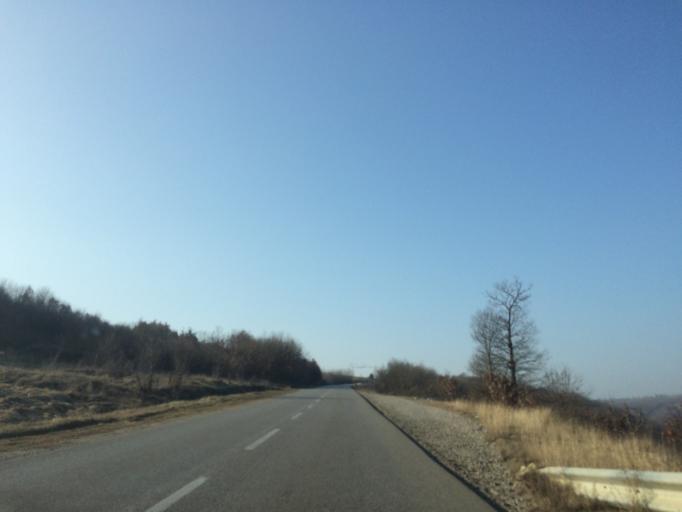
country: XK
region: Pec
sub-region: Komuna e Pejes
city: Kosuriq
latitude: 42.5159
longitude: 20.5543
